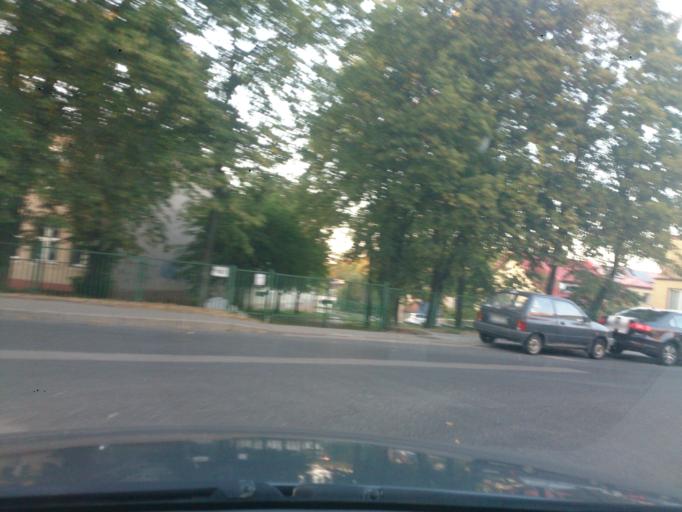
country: PL
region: Pomeranian Voivodeship
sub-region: Gdynia
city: Gdynia
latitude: 54.4926
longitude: 18.5529
